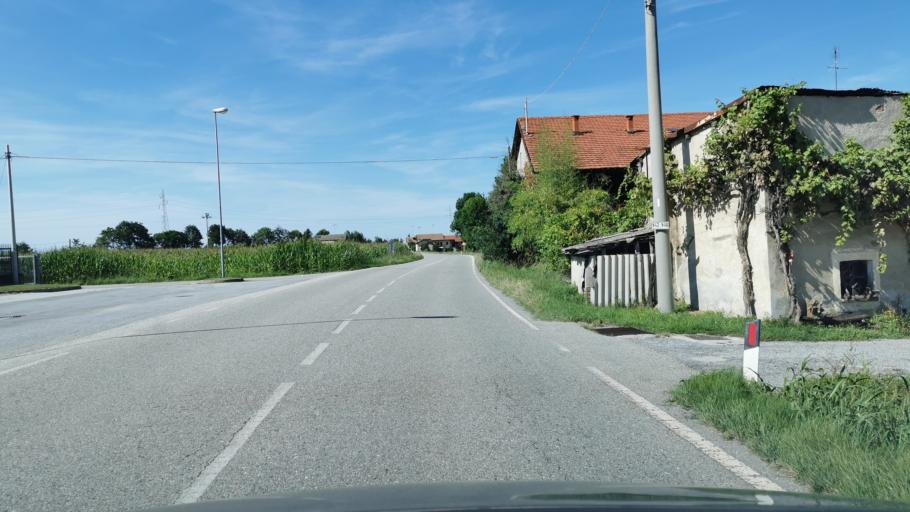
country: IT
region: Piedmont
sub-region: Provincia di Cuneo
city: Boves
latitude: 44.3544
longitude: 7.5593
